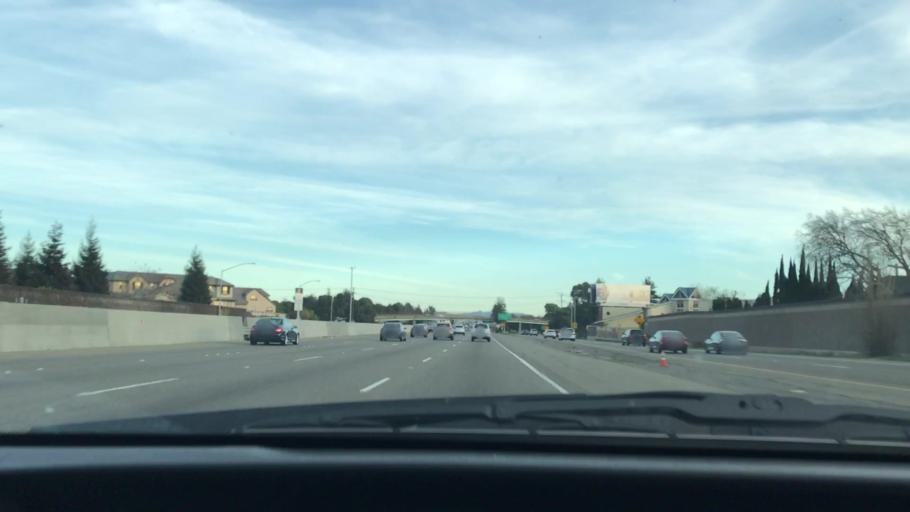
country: US
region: California
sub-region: Alameda County
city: San Lorenzo
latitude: 37.6937
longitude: -122.1426
